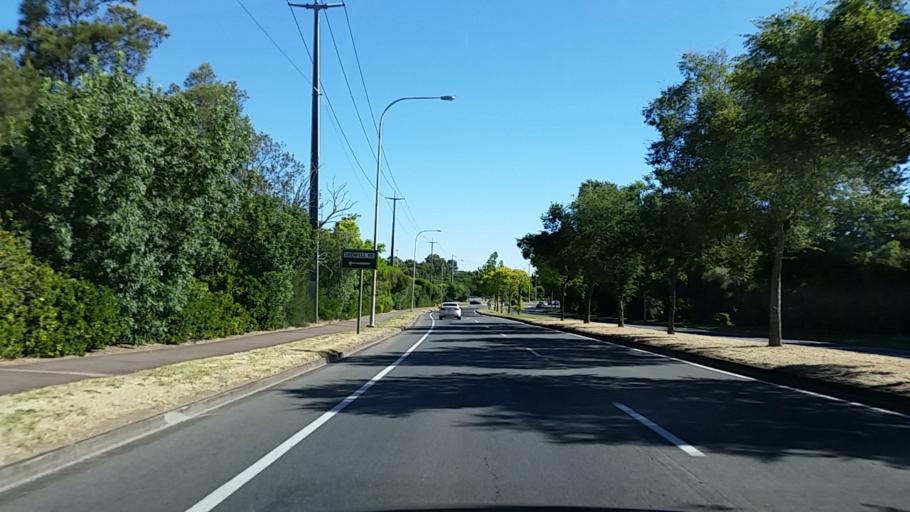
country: AU
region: South Australia
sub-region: Tea Tree Gully
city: Modbury
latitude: -34.8014
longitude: 138.6851
